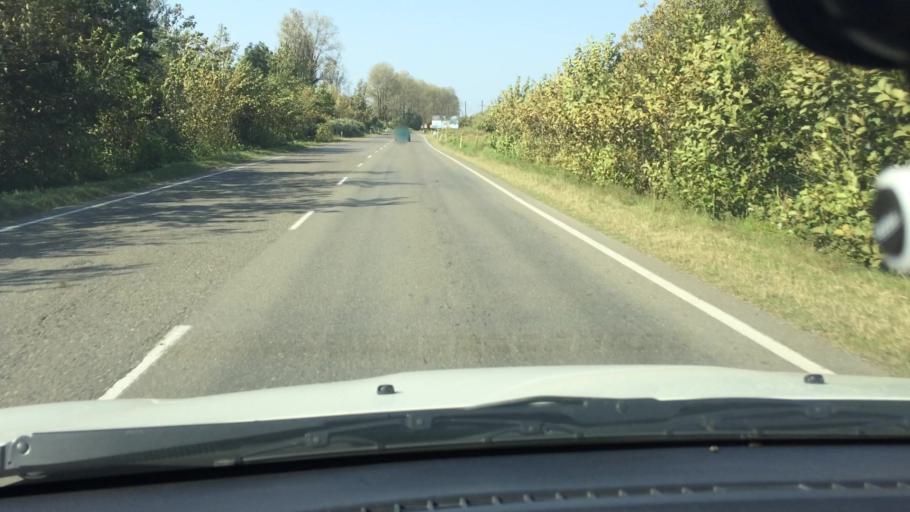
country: GE
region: Guria
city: Urek'i
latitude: 42.0336
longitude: 41.7550
